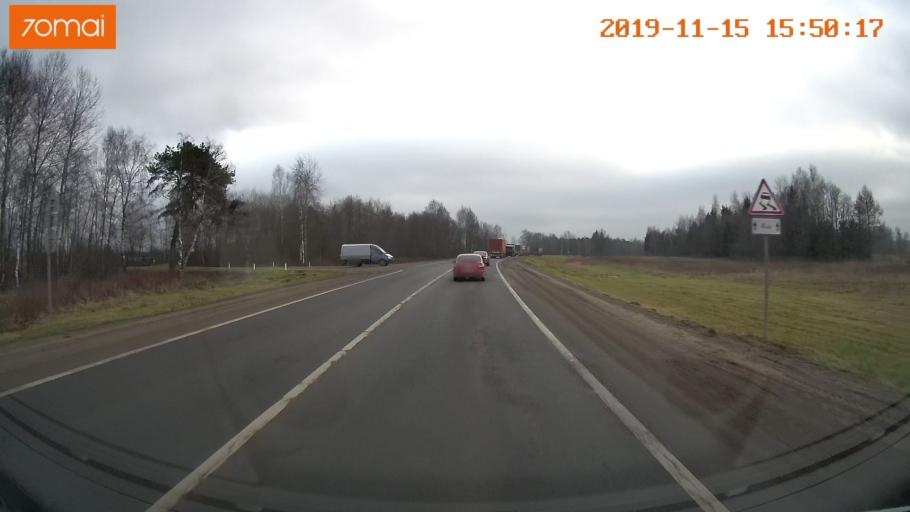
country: RU
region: Jaroslavl
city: Yaroslavl
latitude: 57.9069
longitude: 40.0130
